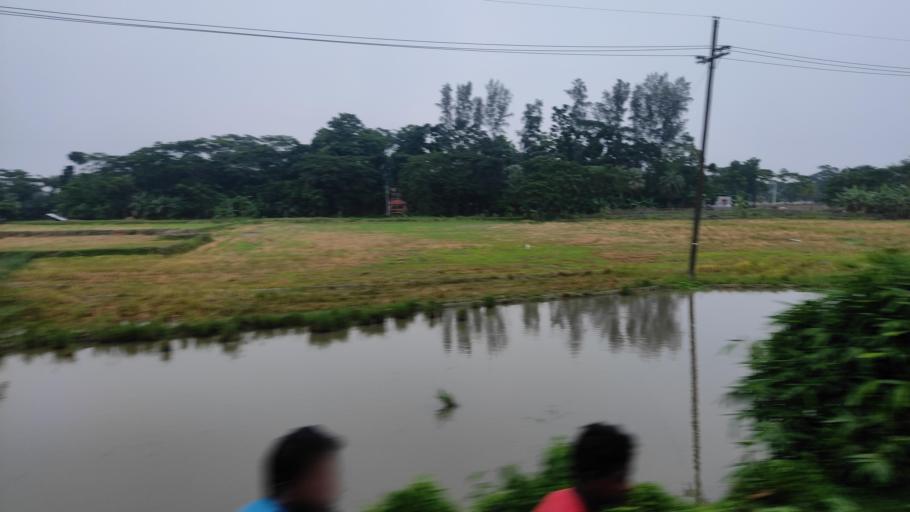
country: BD
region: Barisal
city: Bhandaria
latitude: 22.3199
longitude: 90.3258
